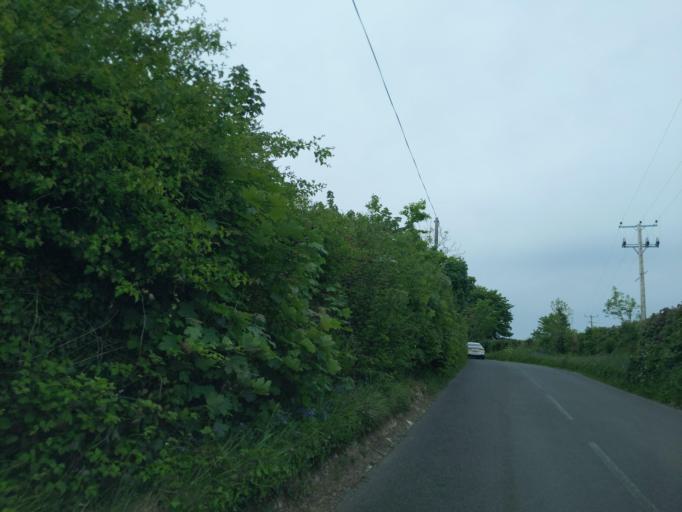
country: GB
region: England
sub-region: Devon
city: Plympton
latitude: 50.4144
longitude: -4.0470
